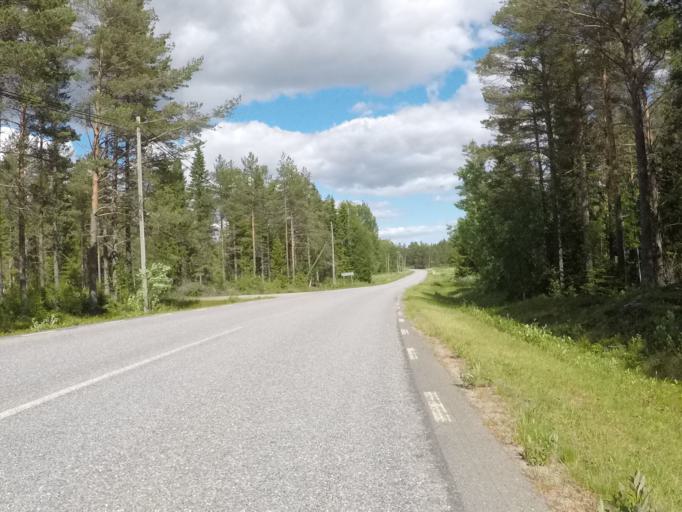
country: SE
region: Vaesterbotten
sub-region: Robertsfors Kommun
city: Robertsfors
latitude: 63.9637
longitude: 20.8091
